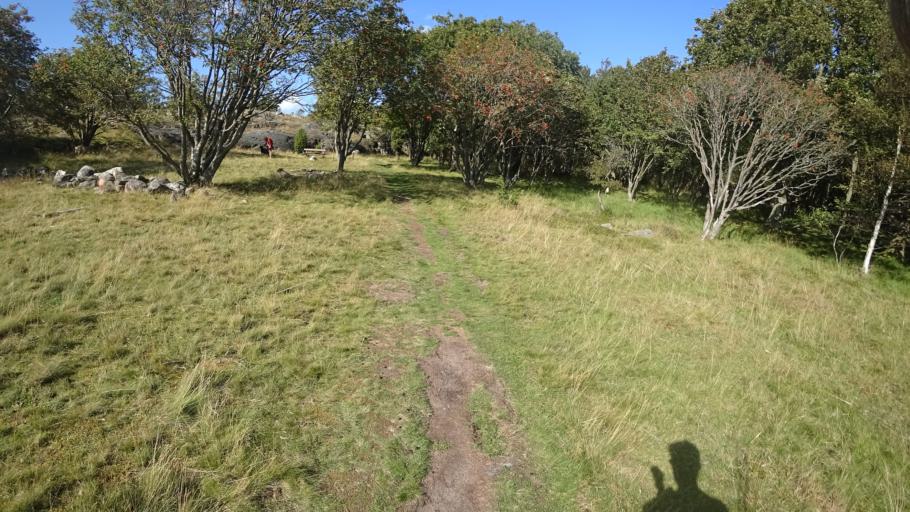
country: SE
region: Vaestra Goetaland
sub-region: Goteborg
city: Styrso
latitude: 57.6027
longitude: 11.7738
